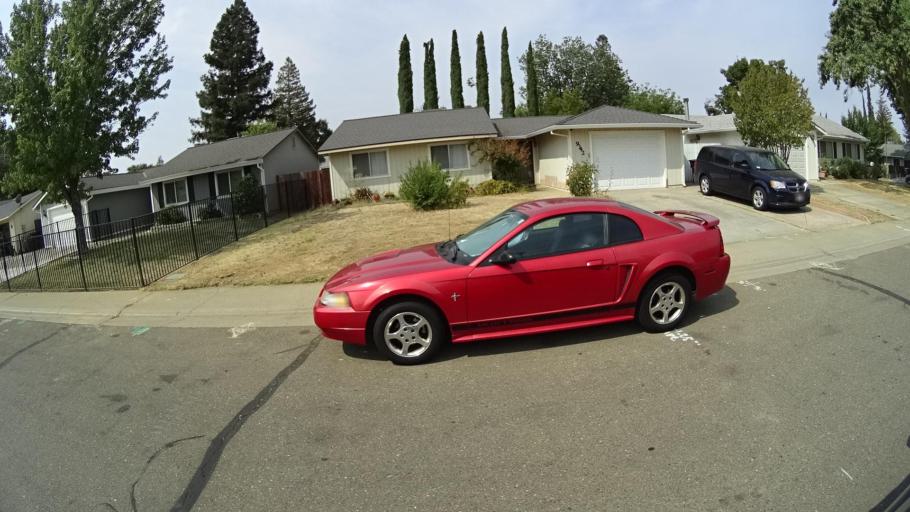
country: US
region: California
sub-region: Sacramento County
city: Elk Grove
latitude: 38.4184
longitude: -121.3805
